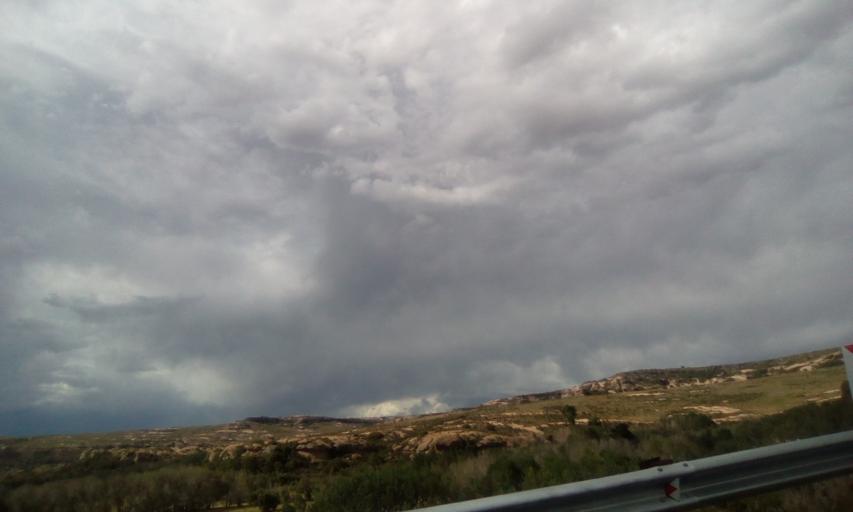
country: ZA
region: Orange Free State
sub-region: Thabo Mofutsanyana District Municipality
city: Ladybrand
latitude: -29.2495
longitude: 27.4352
